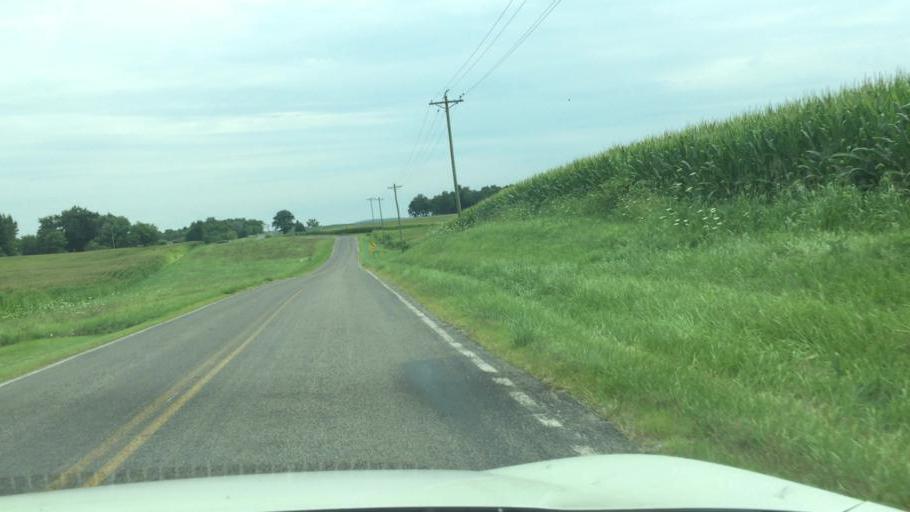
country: US
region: Ohio
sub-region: Champaign County
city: Mechanicsburg
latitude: 40.0501
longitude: -83.6565
